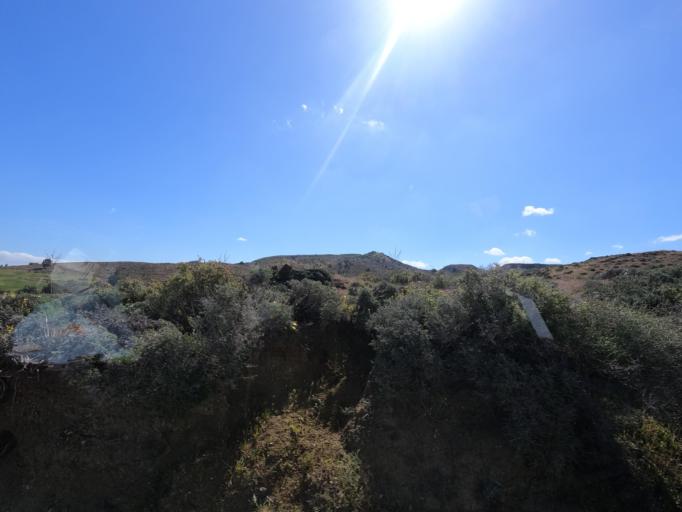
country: CY
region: Lefkosia
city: Peristerona
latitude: 35.0658
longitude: 33.0587
